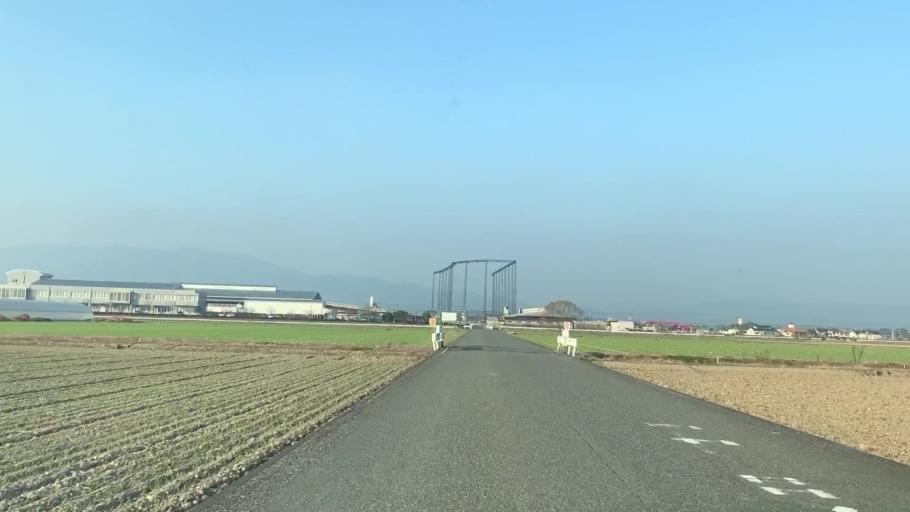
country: JP
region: Saga Prefecture
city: Saga-shi
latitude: 33.2607
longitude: 130.2482
